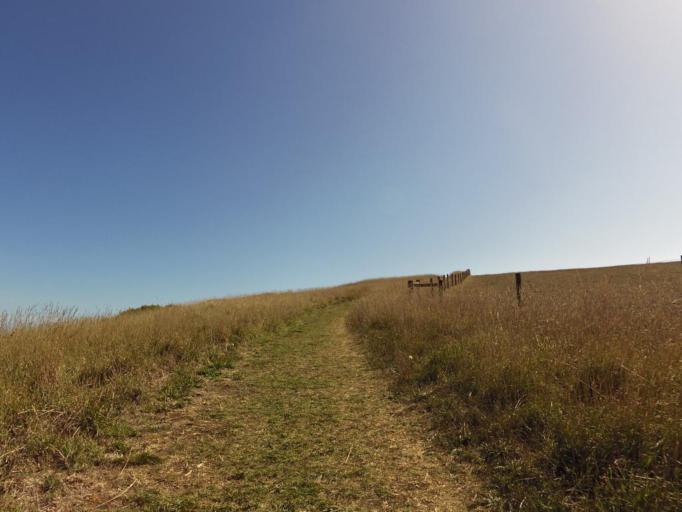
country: AU
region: Victoria
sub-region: Bass Coast
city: North Wonthaggi
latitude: -38.5372
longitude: 145.4310
